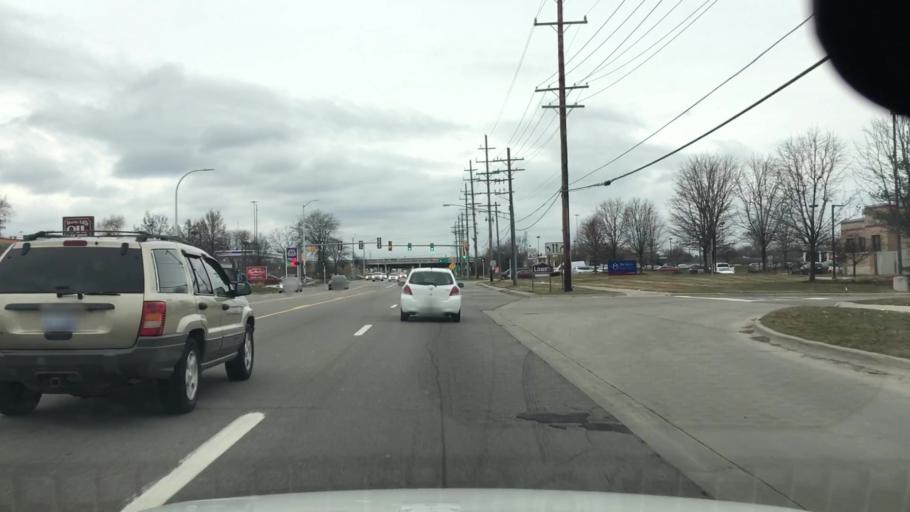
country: US
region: Michigan
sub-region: Oakland County
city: Madison Heights
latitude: 42.5048
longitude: -83.1094
